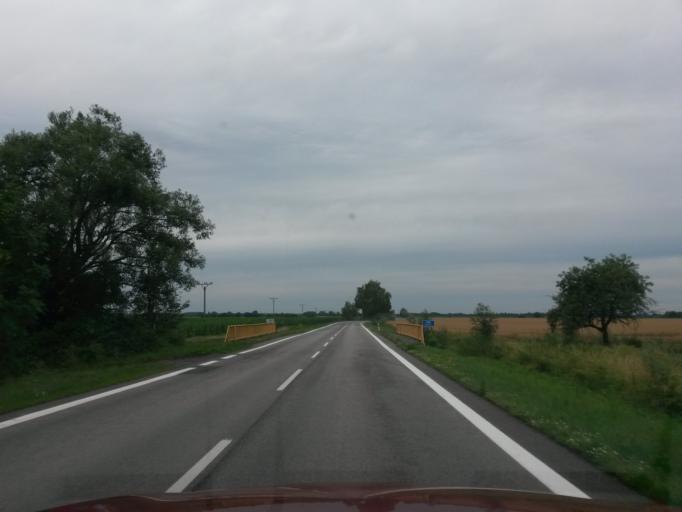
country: SK
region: Nitriansky
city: Zeliezovce
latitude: 48.1240
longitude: 18.6935
